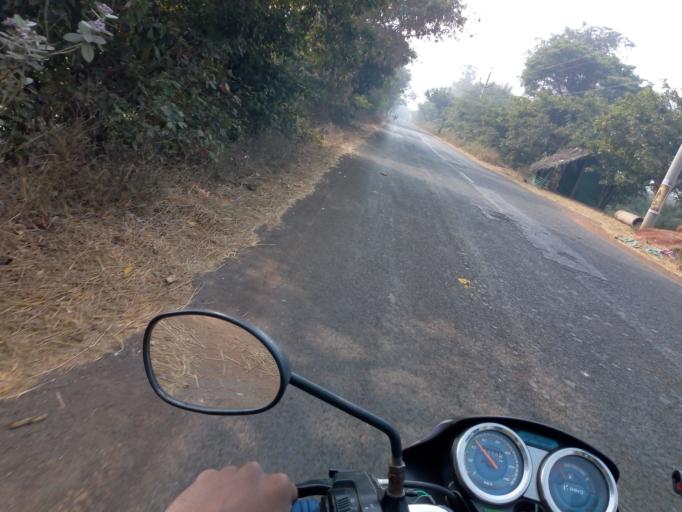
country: IN
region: Andhra Pradesh
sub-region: West Godavari
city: Tadepallegudem
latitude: 16.7675
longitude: 81.4250
